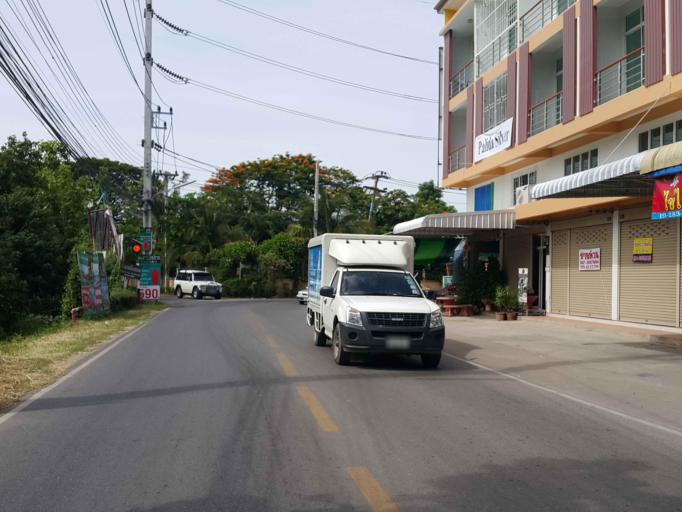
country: TH
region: Chiang Mai
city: Chiang Mai
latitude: 18.7731
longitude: 98.9940
